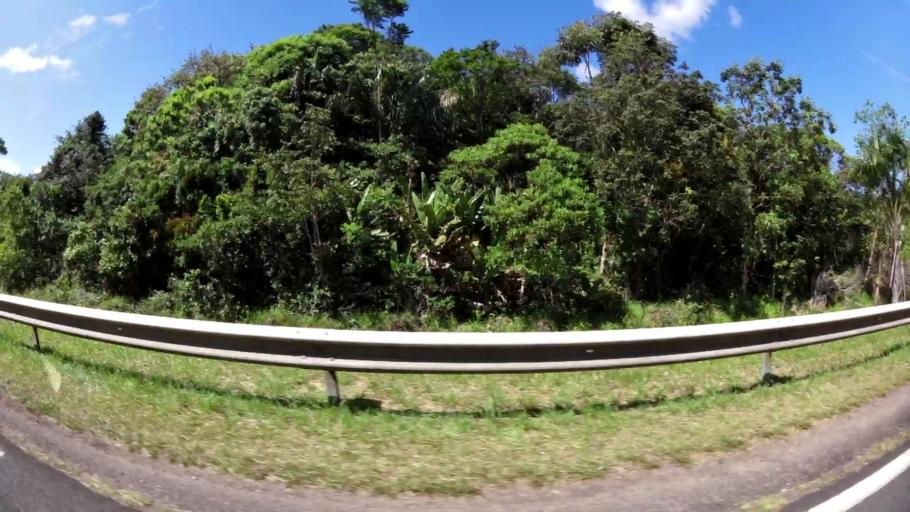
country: GF
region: Guyane
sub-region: Guyane
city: Matoury
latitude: 4.8348
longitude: -52.3312
